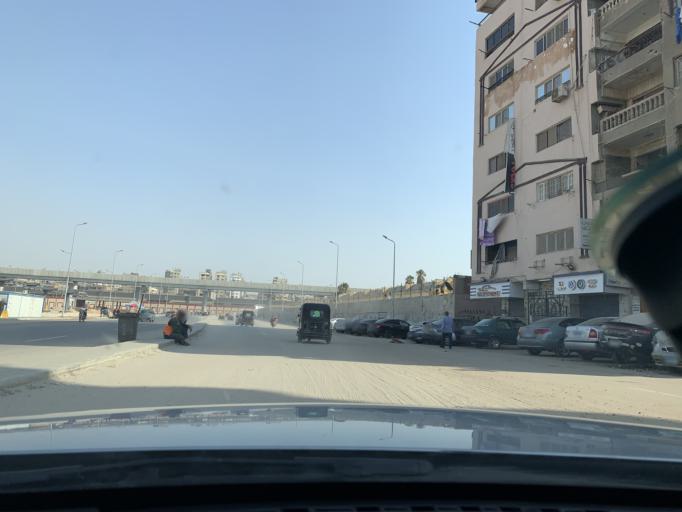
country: EG
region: Muhafazat al Qalyubiyah
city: Al Khankah
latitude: 30.1311
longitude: 31.3658
